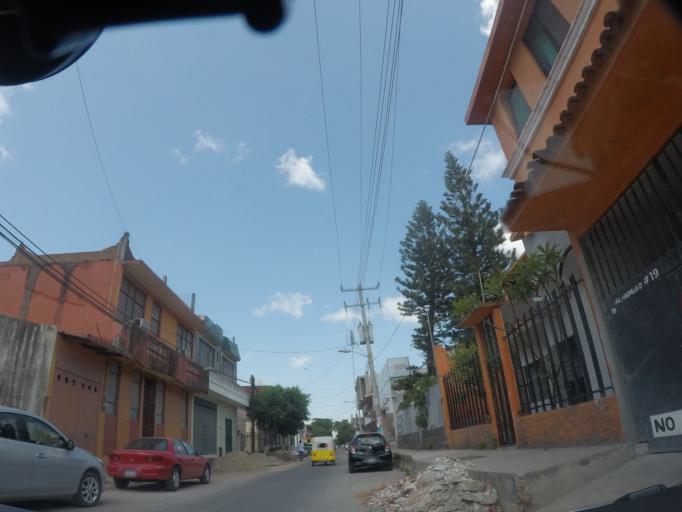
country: MX
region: Oaxaca
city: Juchitan de Zaragoza
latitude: 16.4350
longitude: -95.0206
